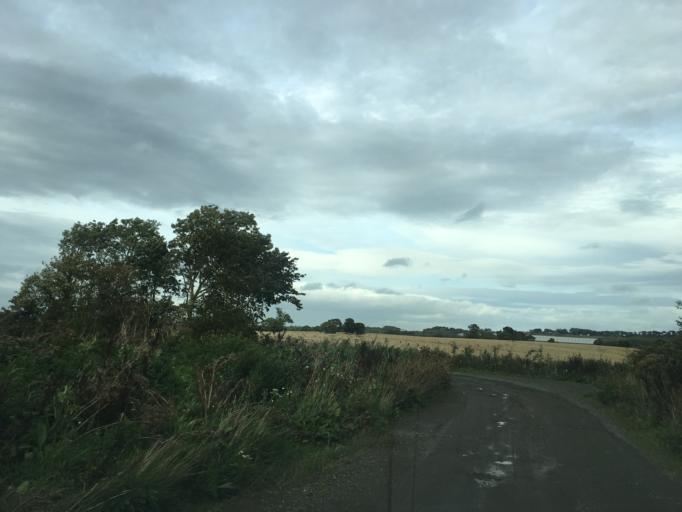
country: GB
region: Scotland
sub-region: West Lothian
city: Kirknewton
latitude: 55.9111
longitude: -3.4264
